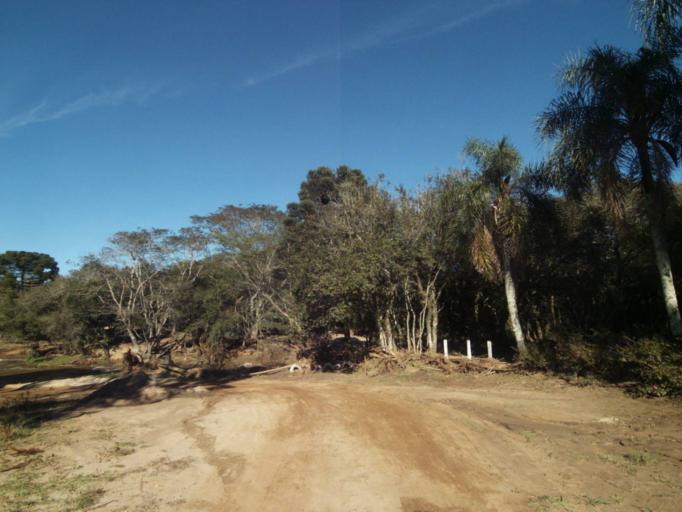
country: BR
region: Parana
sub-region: Tibagi
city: Tibagi
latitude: -24.5478
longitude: -50.3685
